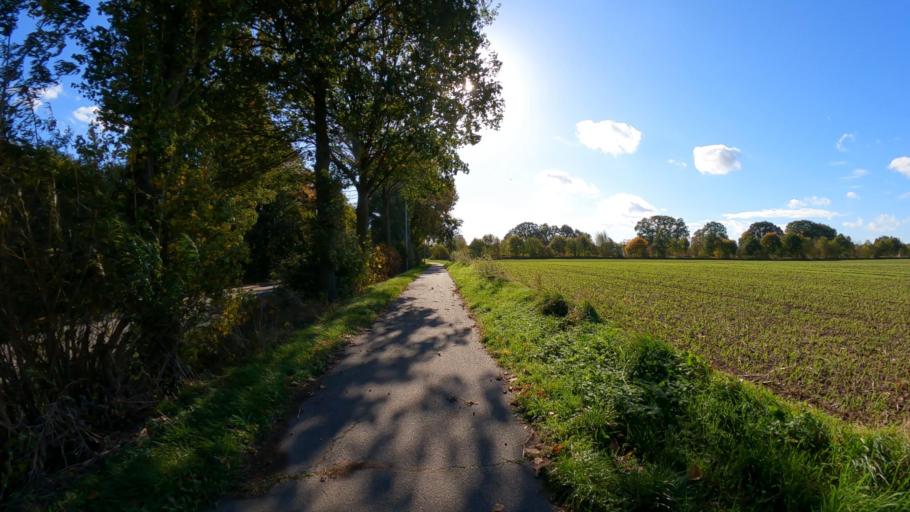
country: DE
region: Schleswig-Holstein
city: Ahrensburg
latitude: 53.6872
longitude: 10.2260
